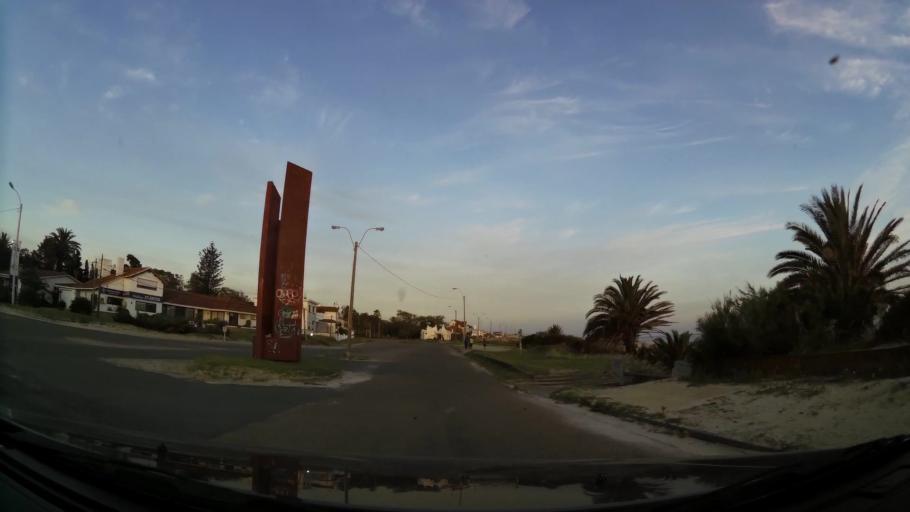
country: UY
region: Canelones
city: Atlantida
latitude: -34.7799
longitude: -55.7571
